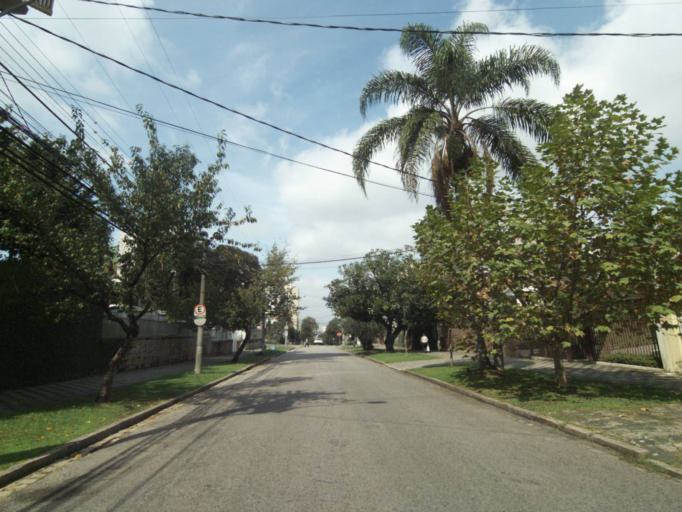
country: BR
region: Parana
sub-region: Curitiba
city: Curitiba
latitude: -25.4302
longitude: -49.2597
